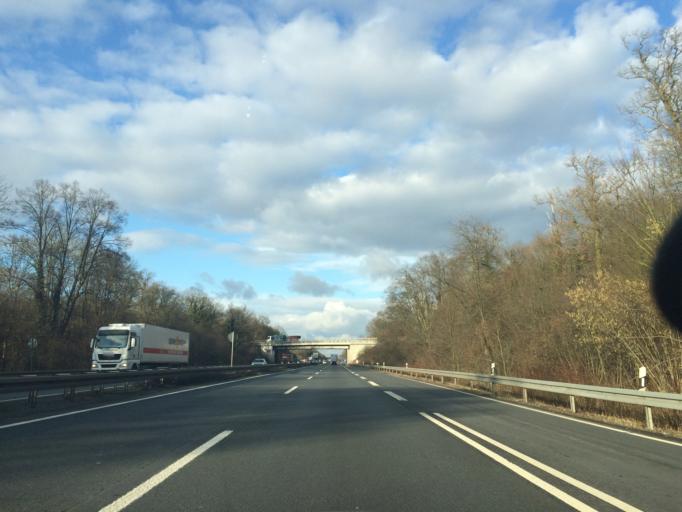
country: DE
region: Hesse
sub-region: Regierungsbezirk Darmstadt
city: Alsbach-Hahnlein
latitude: 49.7423
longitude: 8.5434
